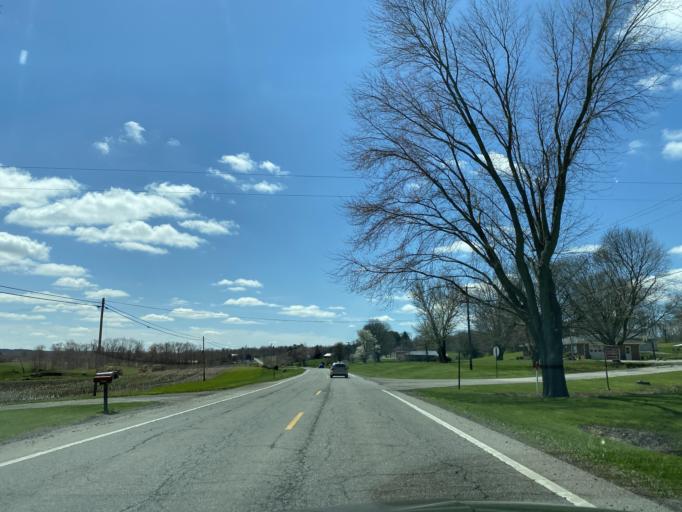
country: US
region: Ohio
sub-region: Wayne County
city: Shreve
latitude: 40.7051
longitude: -82.0153
